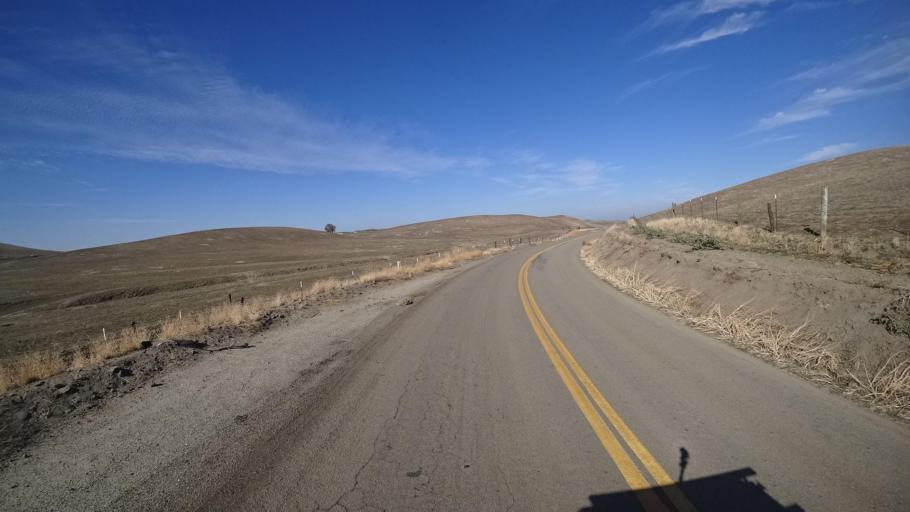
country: US
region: California
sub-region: Kern County
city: Oildale
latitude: 35.6301
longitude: -118.9454
